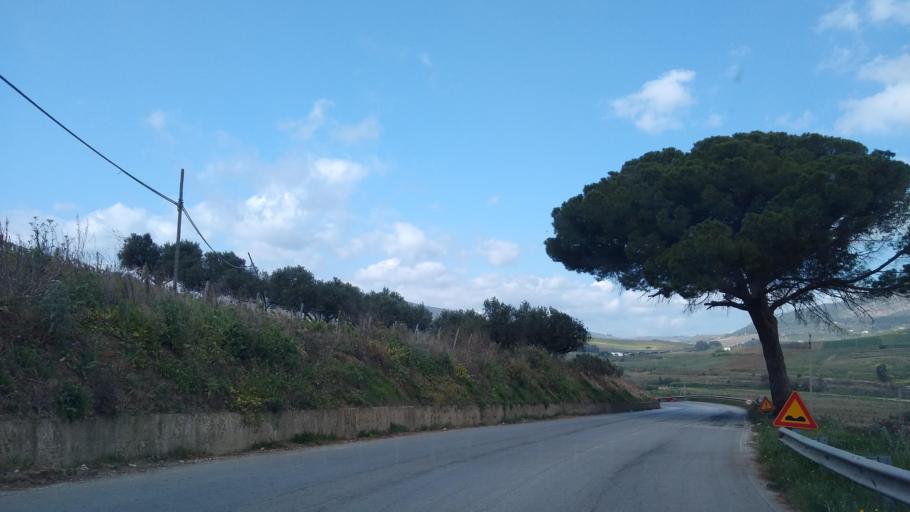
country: IT
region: Sicily
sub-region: Trapani
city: Alcamo
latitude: 37.9715
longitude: 12.9247
